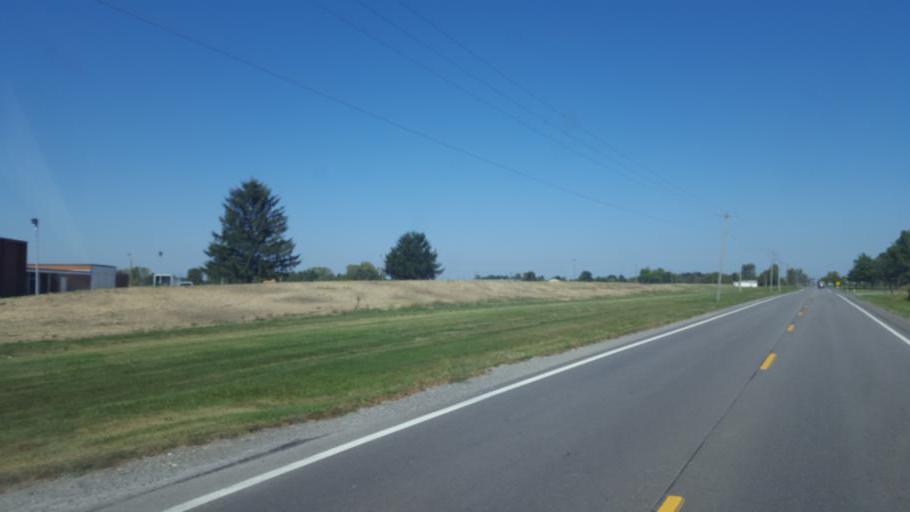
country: US
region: Ohio
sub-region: Marion County
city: Marion
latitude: 40.6099
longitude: -83.0317
